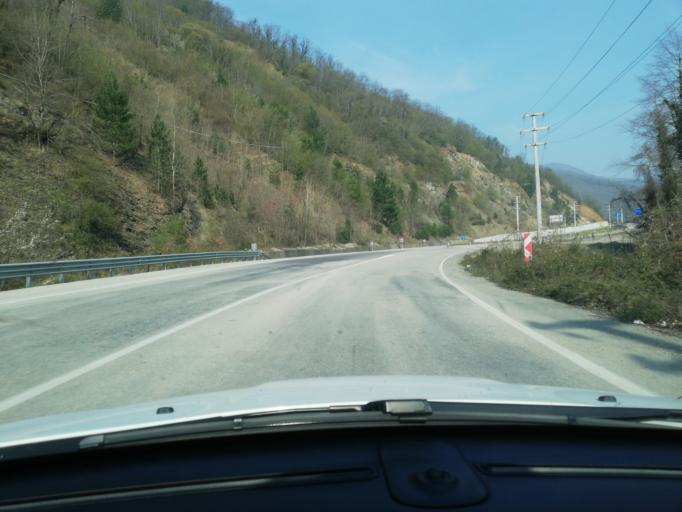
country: TR
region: Karabuk
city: Yenice
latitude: 41.2040
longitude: 32.3671
